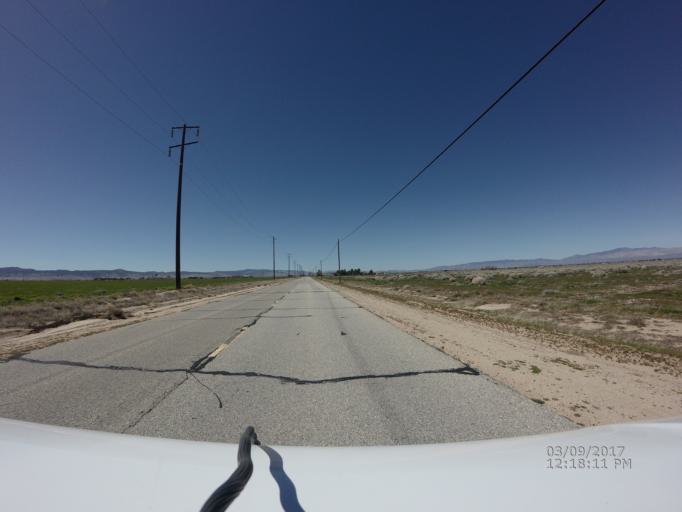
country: US
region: California
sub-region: Los Angeles County
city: Quartz Hill
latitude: 34.7330
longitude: -118.2574
